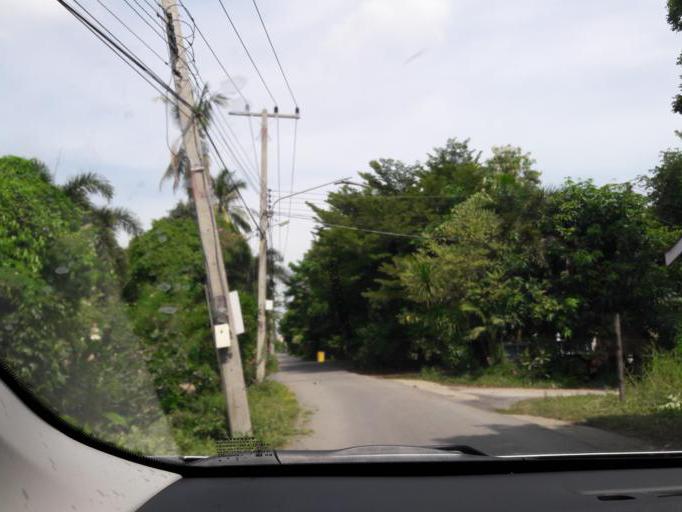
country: TH
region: Ang Thong
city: Ang Thong
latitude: 14.5742
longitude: 100.4410
